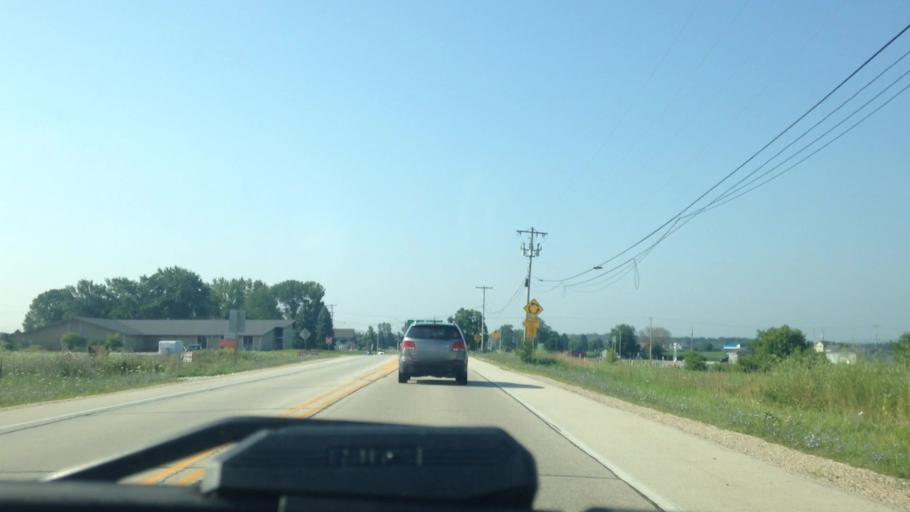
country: US
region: Wisconsin
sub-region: Waukesha County
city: Merton
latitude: 43.1963
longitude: -88.2614
